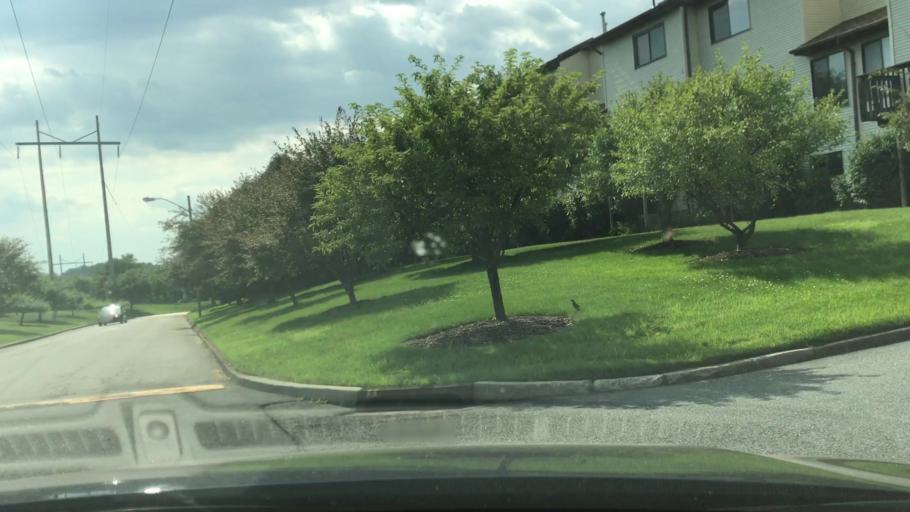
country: US
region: New York
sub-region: Rockland County
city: Spring Valley
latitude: 41.1138
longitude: -74.0235
